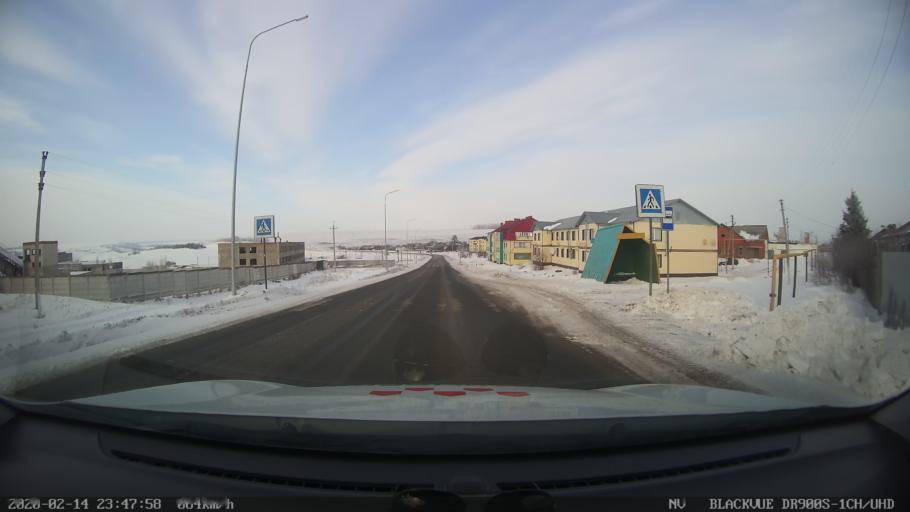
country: RU
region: Tatarstan
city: Kuybyshevskiy Zaton
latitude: 55.2446
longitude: 49.2064
